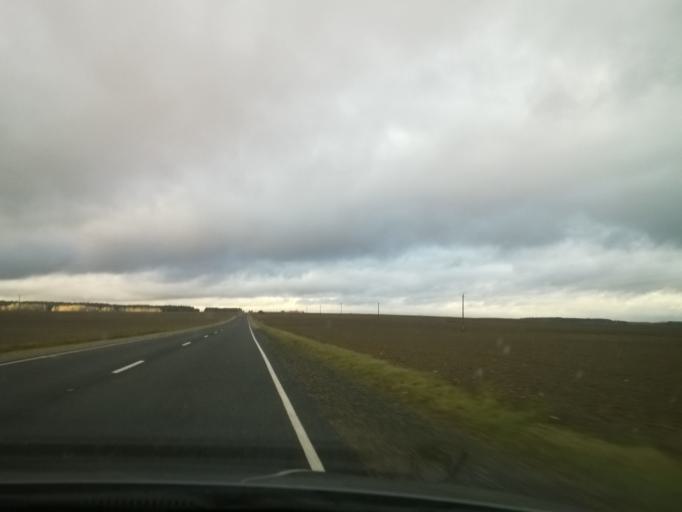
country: BY
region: Grodnenskaya
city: Mir
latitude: 53.4199
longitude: 26.4883
